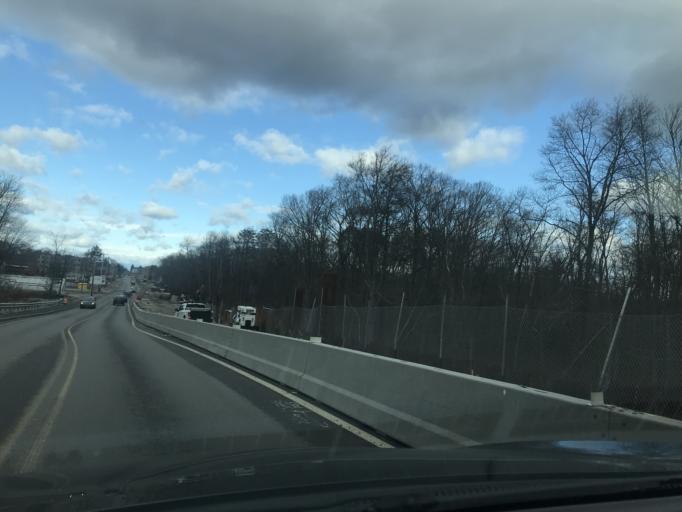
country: US
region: Massachusetts
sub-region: Plymouth County
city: Rockland
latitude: 42.1590
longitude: -70.9552
